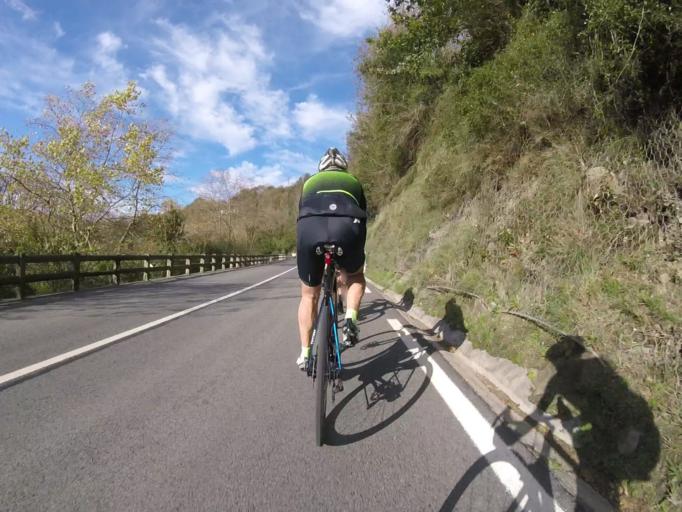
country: ES
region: Basque Country
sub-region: Provincia de Guipuzcoa
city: Usurbil
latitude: 43.2828
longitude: -2.0762
